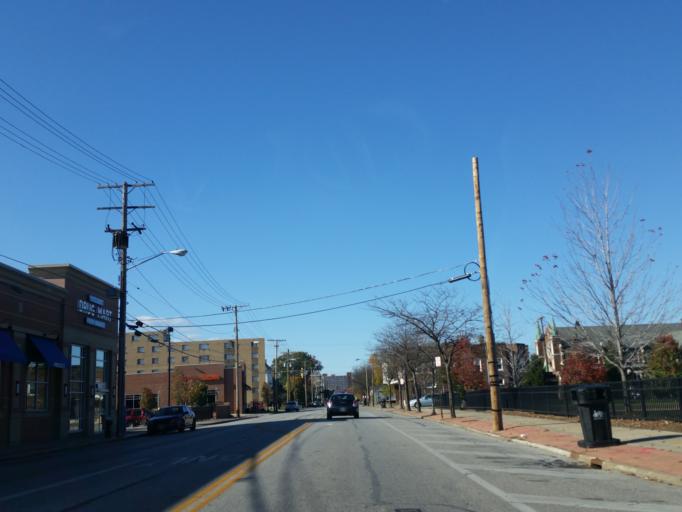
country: US
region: Ohio
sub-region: Cuyahoga County
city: Lakewood
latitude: 41.4846
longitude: -81.7792
